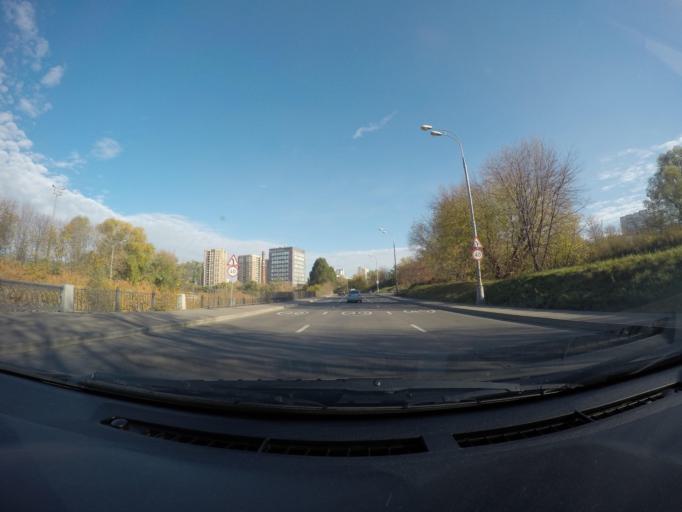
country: RU
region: Moskovskaya
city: Bogorodskoye
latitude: 55.8048
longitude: 37.7017
